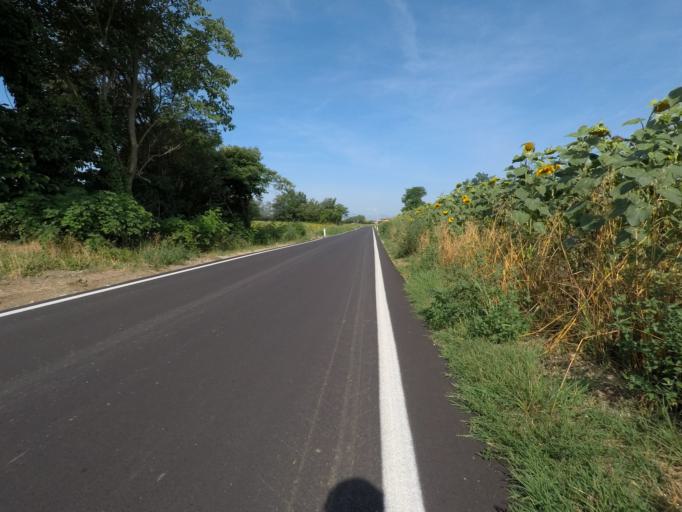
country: IT
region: Friuli Venezia Giulia
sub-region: Provincia di Udine
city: San Vito di Fagagna
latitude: 46.0666
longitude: 13.0908
